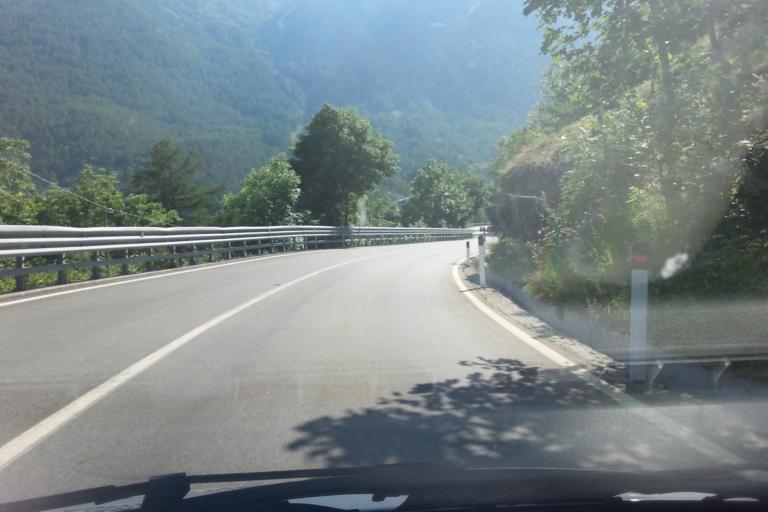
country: IT
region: Piedmont
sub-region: Provincia di Torino
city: Moncenisio
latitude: 45.1912
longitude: 6.9840
